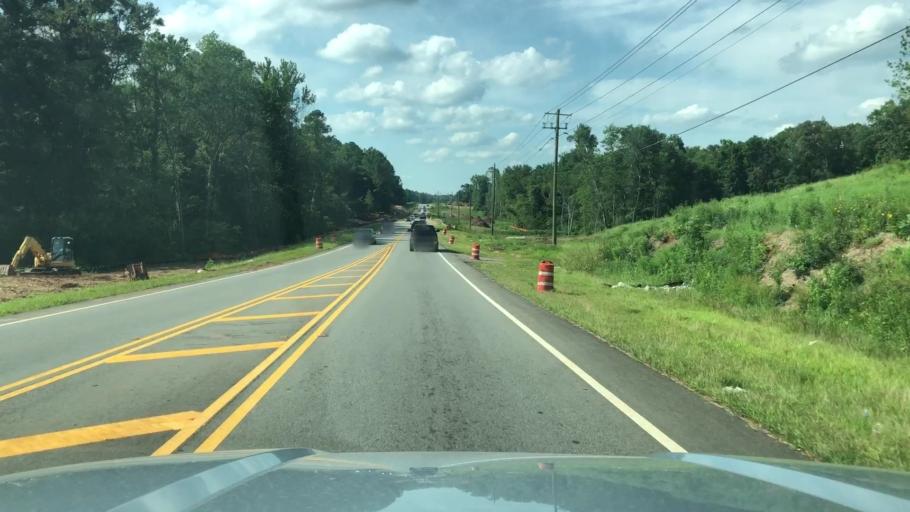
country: US
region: Georgia
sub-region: Paulding County
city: Hiram
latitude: 33.8166
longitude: -84.7584
